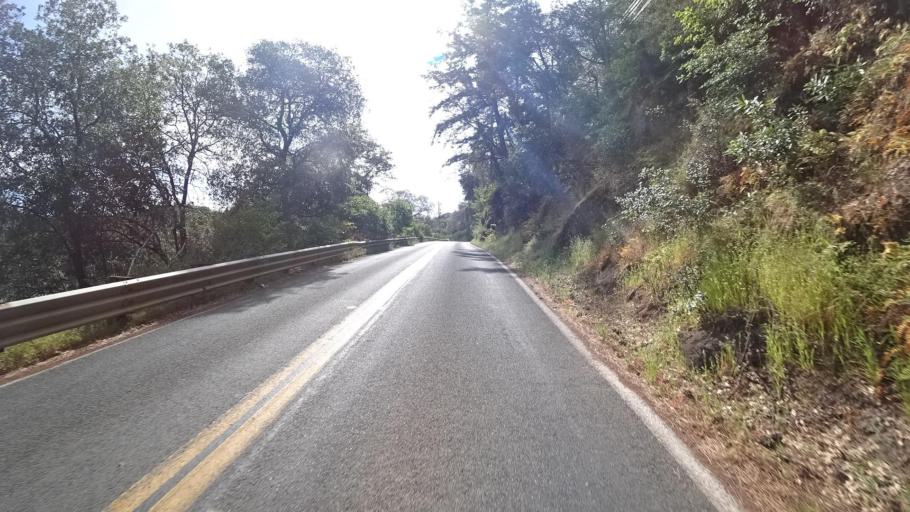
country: US
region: California
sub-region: Lake County
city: Soda Bay
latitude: 39.0047
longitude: -122.7646
